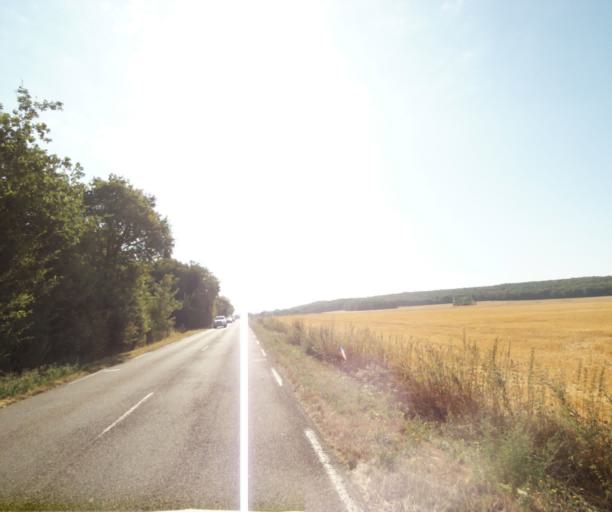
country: FR
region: Ile-de-France
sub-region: Departement de l'Essonne
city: Bouray-sur-Juine
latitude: 48.5150
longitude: 2.3138
